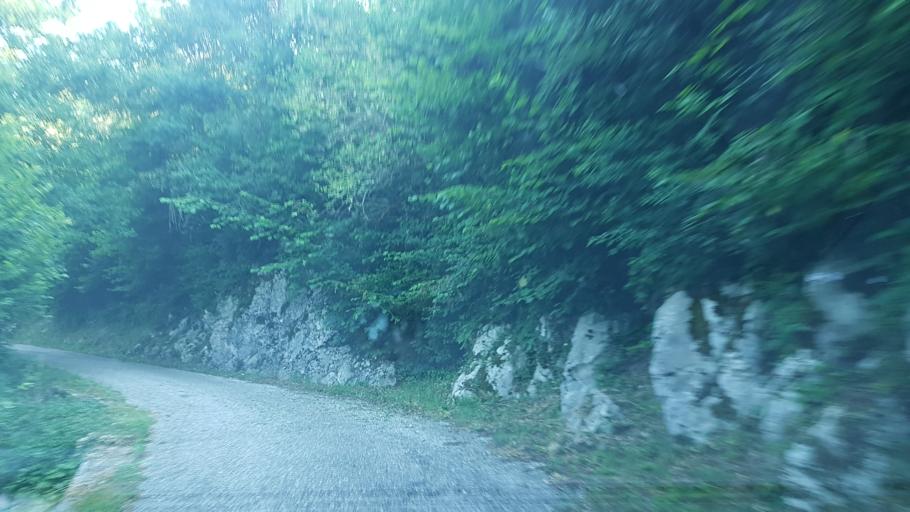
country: IT
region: Friuli Venezia Giulia
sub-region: Provincia di Udine
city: Nimis
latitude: 46.2314
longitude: 13.2550
